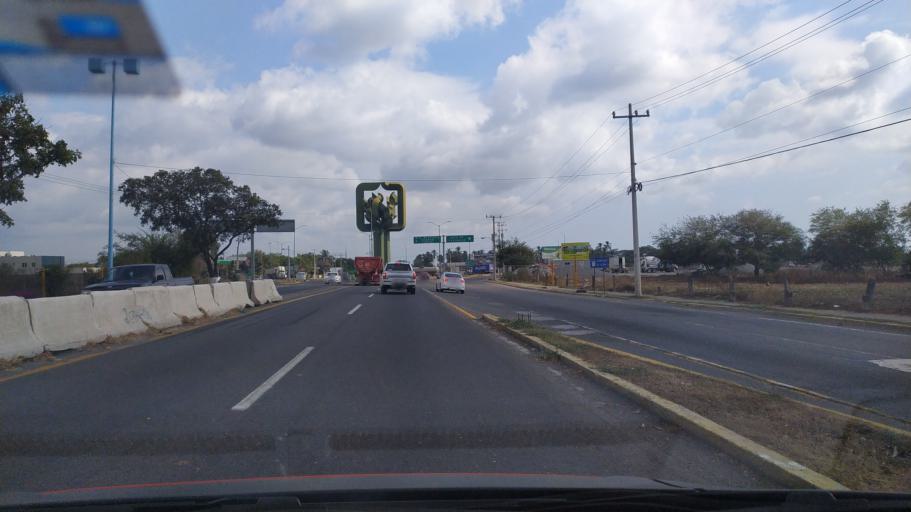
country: MX
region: Colima
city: Tecoman
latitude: 18.9419
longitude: -103.8960
